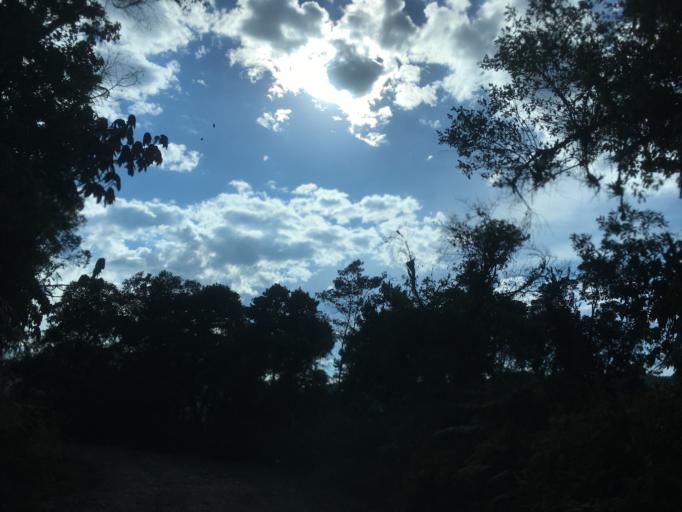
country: CO
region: Santander
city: Oiba
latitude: 6.1275
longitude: -73.1954
